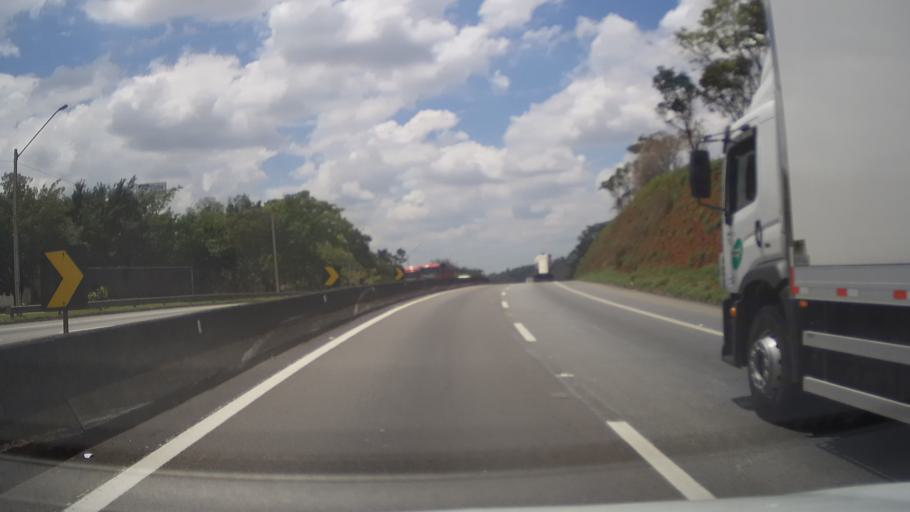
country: BR
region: Minas Gerais
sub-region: Tres Coracoes
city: Tres Coracoes
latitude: -21.6972
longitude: -45.3654
